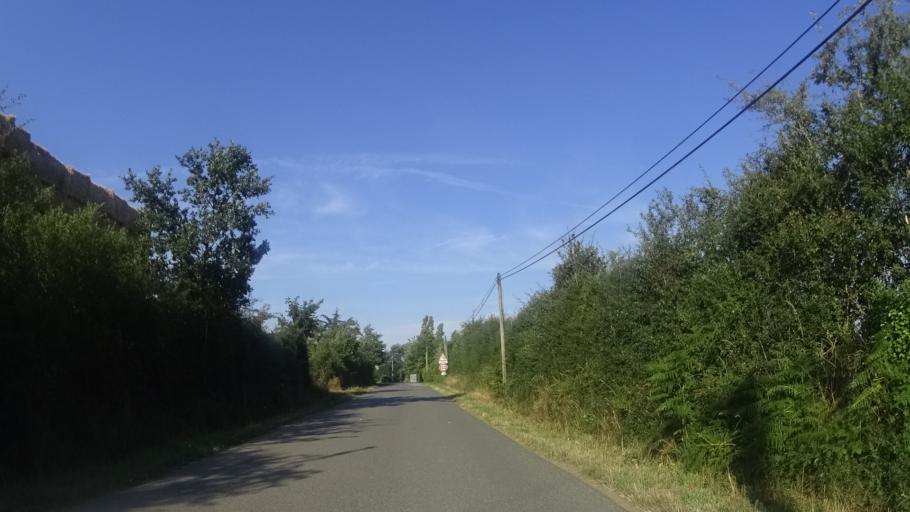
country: FR
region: Pays de la Loire
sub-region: Departement de la Loire-Atlantique
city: Mouzeil
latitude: 47.4882
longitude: -1.3712
